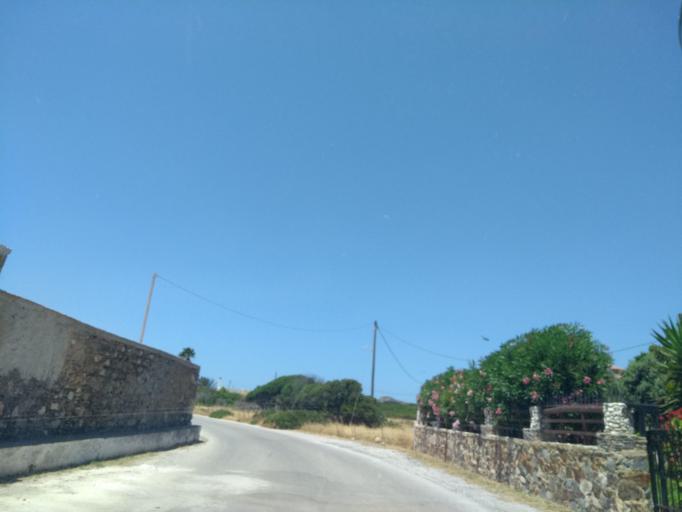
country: GR
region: Crete
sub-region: Nomos Chanias
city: Vryses
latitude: 35.3585
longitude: 23.5323
